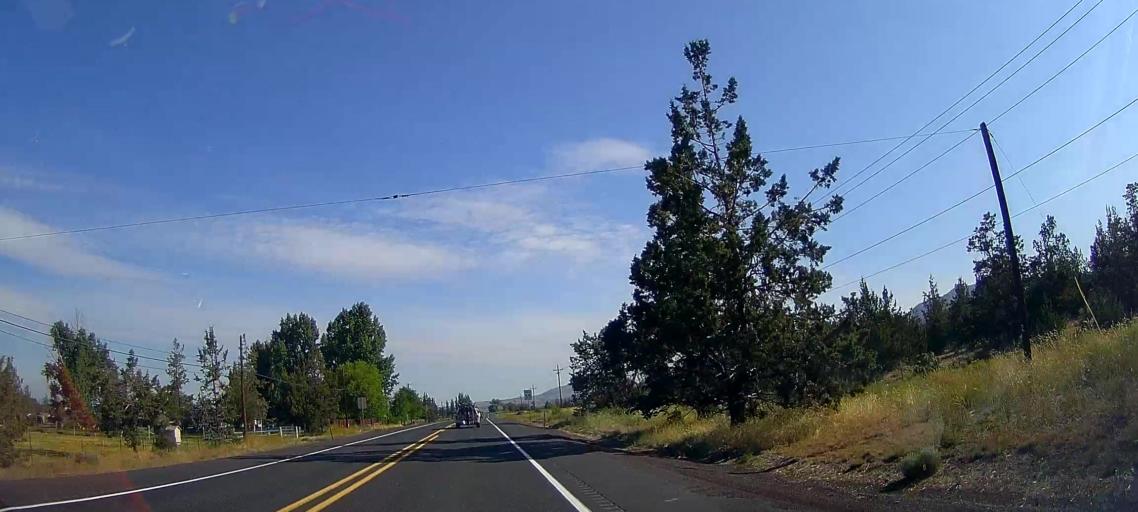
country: US
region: Oregon
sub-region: Deschutes County
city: Terrebonne
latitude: 44.3636
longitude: -121.1785
